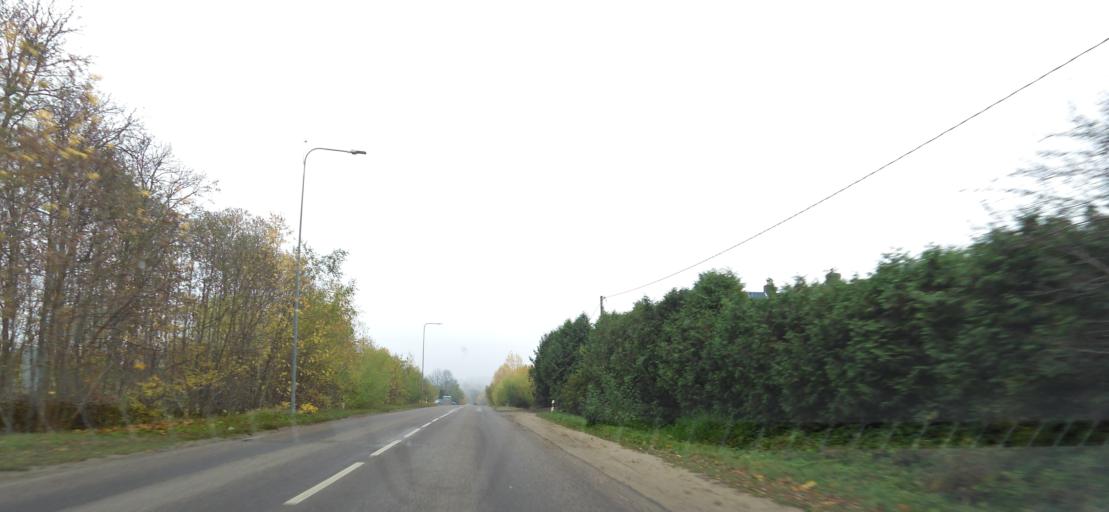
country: LT
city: Skaidiskes
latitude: 54.6584
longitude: 25.3681
